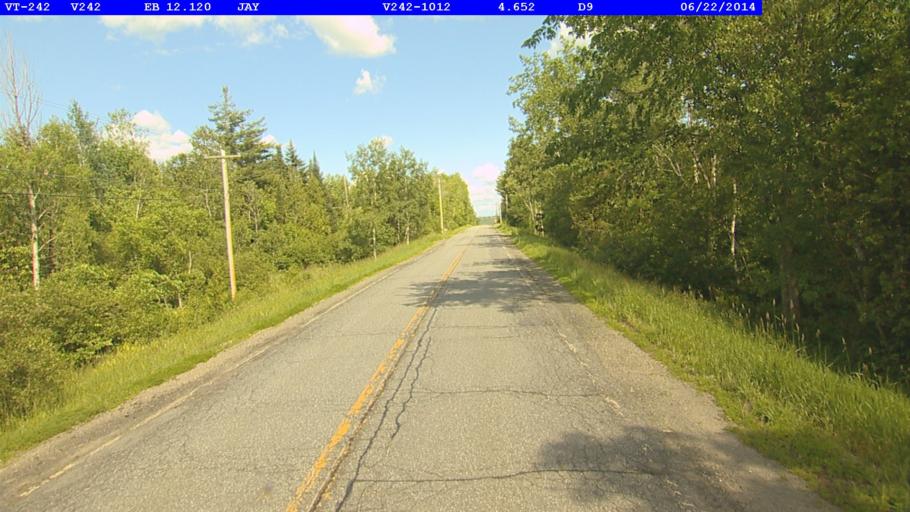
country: US
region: Vermont
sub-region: Orleans County
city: Newport
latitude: 44.9488
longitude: -72.4264
